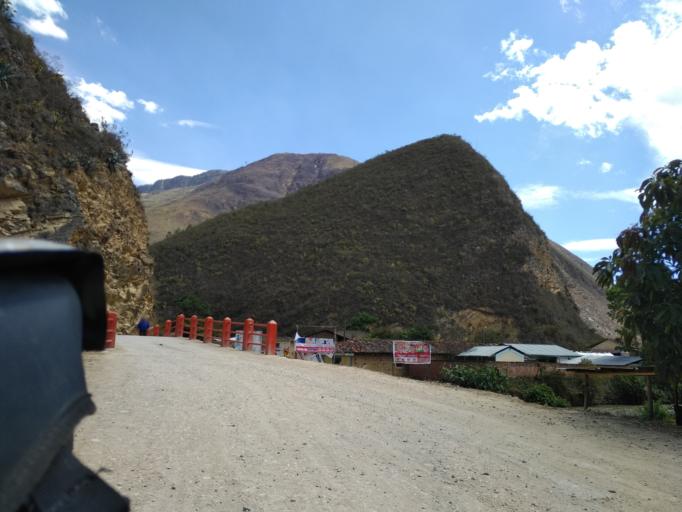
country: PE
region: Amazonas
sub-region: Provincia de Chachapoyas
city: Duraznopampa
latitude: -6.5604
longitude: -77.8294
